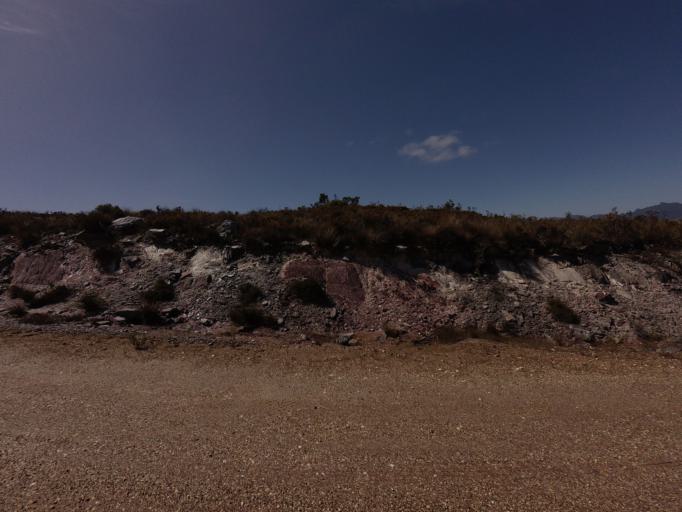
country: AU
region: Tasmania
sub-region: Huon Valley
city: Geeveston
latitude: -43.0380
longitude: 146.2748
